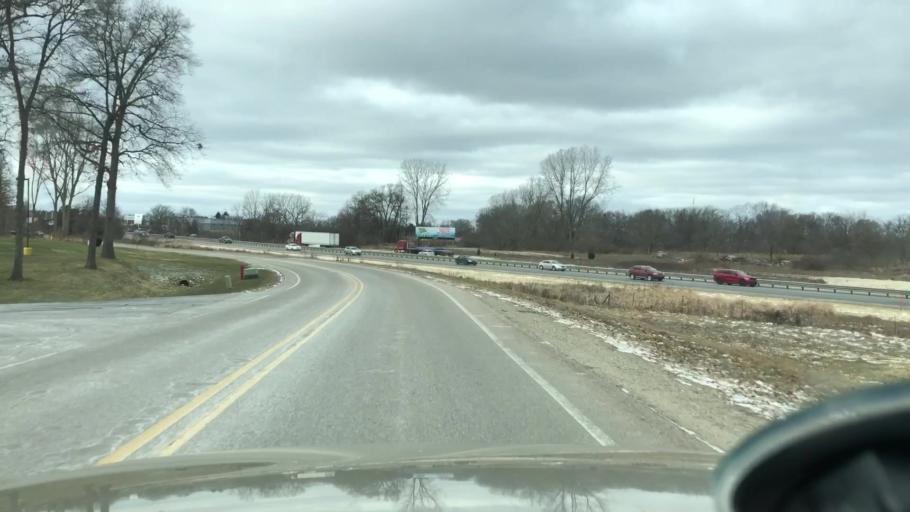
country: US
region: Michigan
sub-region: Jackson County
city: Jackson
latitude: 42.2761
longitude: -84.3657
